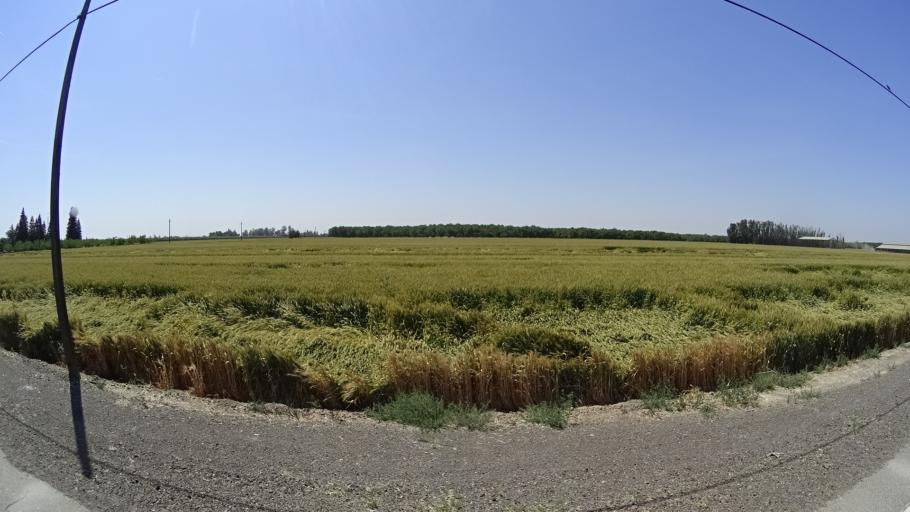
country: US
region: California
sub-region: Fresno County
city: Laton
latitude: 36.4016
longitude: -119.7006
